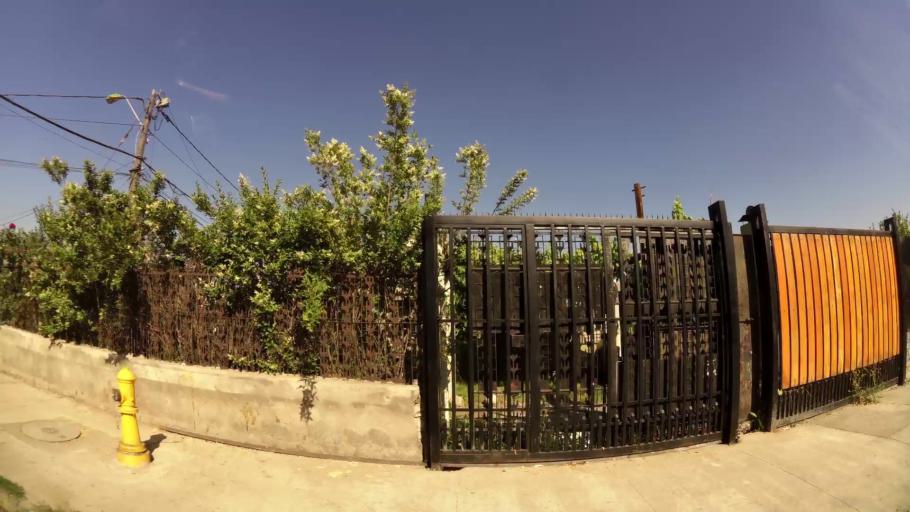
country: CL
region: Santiago Metropolitan
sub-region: Provincia de Maipo
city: San Bernardo
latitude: -33.5716
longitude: -70.6990
